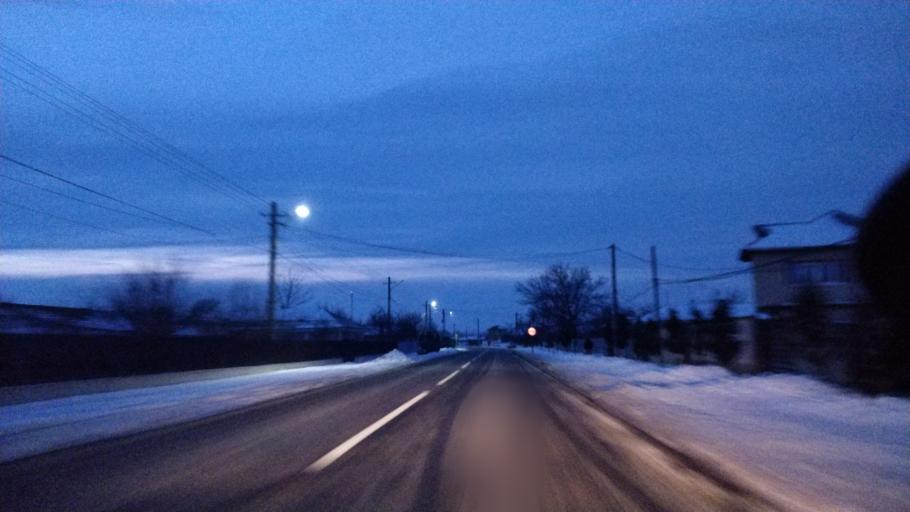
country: RO
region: Vrancea
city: Vulturu de Sus
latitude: 45.6337
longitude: 27.3834
